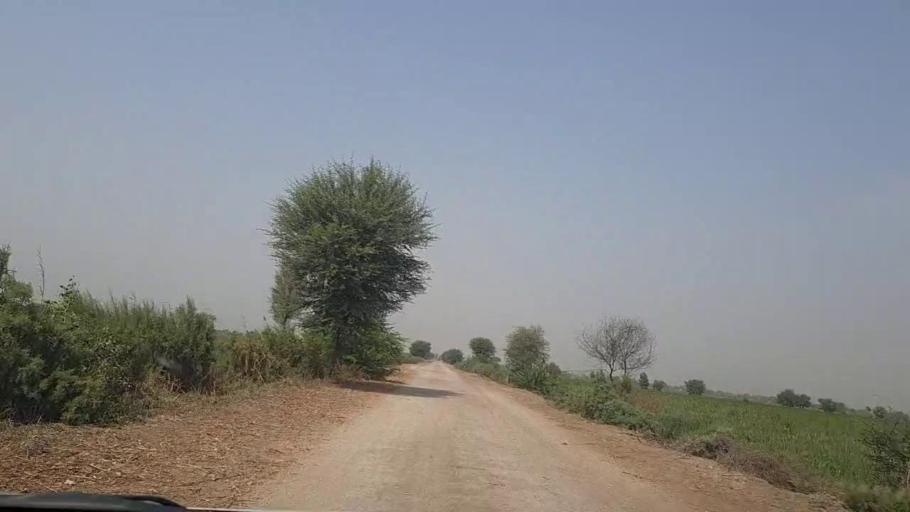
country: PK
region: Sindh
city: Mirpur Khas
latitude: 25.6131
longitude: 69.2009
